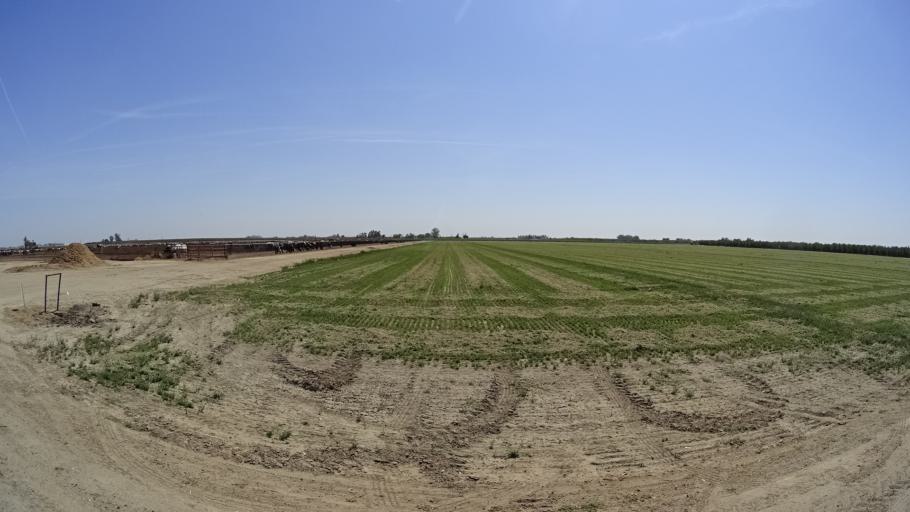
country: US
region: California
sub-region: Fresno County
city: Riverdale
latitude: 36.3932
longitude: -119.8873
